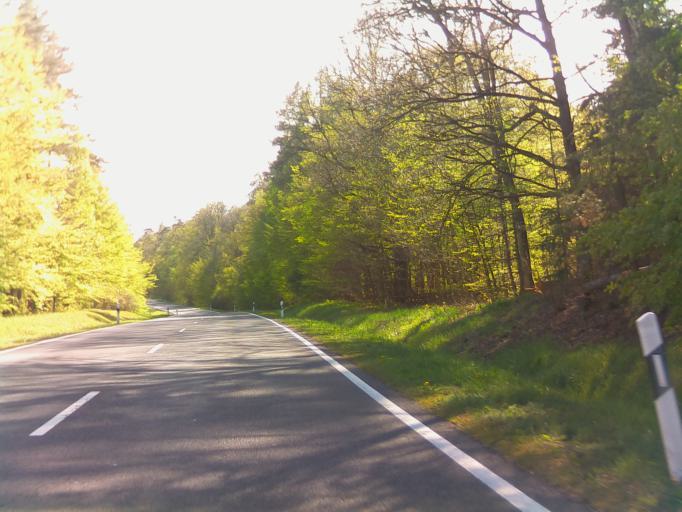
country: DE
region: Bavaria
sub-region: Regierungsbezirk Unterfranken
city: Burgpreppach
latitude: 50.0894
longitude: 10.6575
